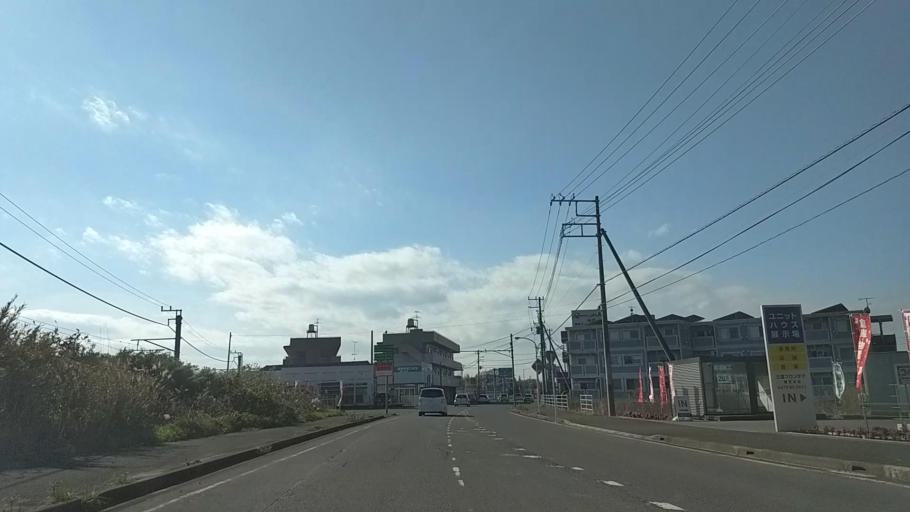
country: JP
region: Chiba
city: Yokaichiba
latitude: 35.6704
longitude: 140.5044
